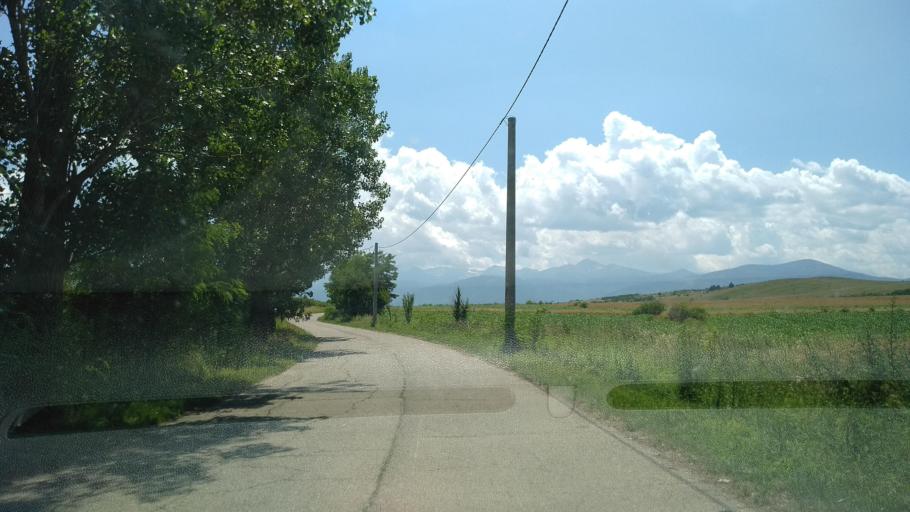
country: RO
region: Hunedoara
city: Densus
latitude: 45.5731
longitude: 22.8095
